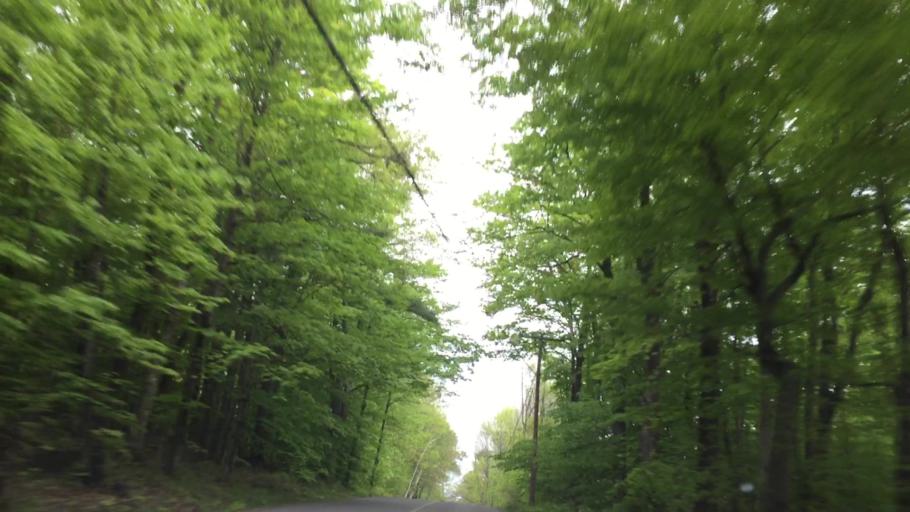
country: US
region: Massachusetts
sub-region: Berkshire County
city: Becket
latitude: 42.2755
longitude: -73.0339
